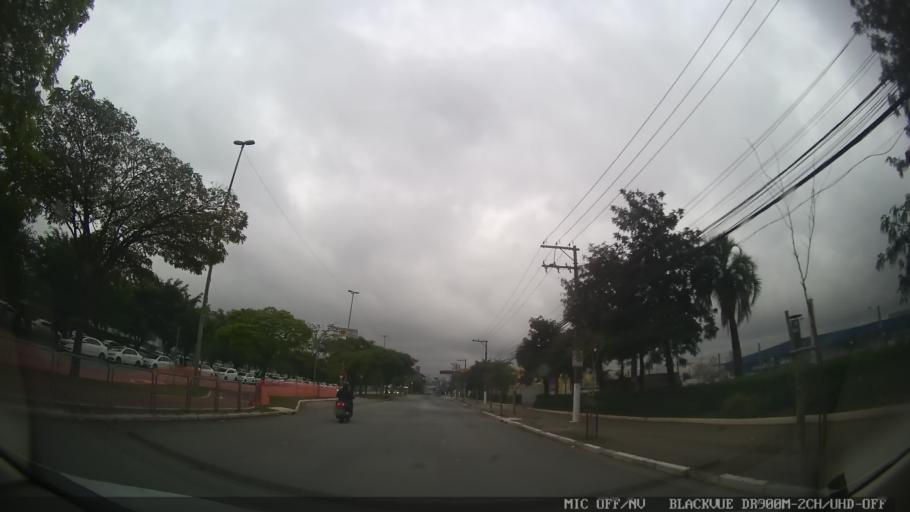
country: BR
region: Sao Paulo
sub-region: Sao Paulo
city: Sao Paulo
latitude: -23.5120
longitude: -46.6158
